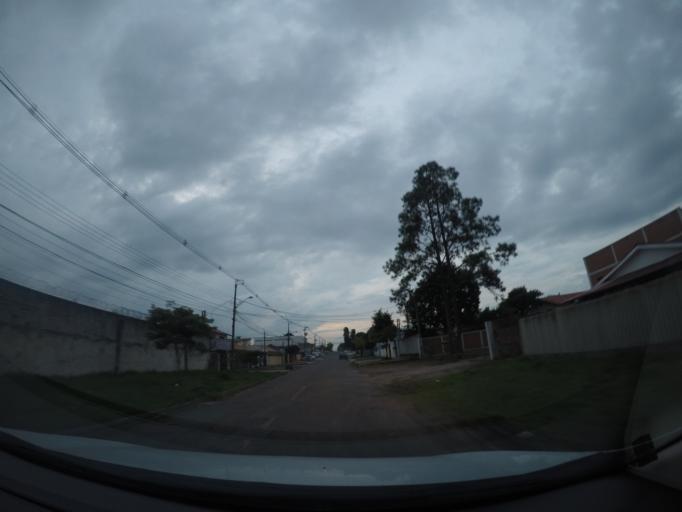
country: BR
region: Parana
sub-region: Sao Jose Dos Pinhais
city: Sao Jose dos Pinhais
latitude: -25.5131
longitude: -49.2236
